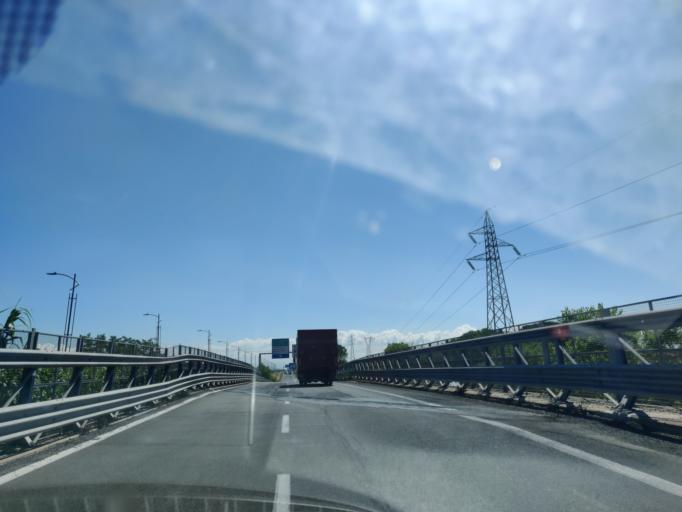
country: IT
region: Latium
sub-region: Citta metropolitana di Roma Capitale
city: Ponte Galeria-La Pisana
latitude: 41.8128
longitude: 12.3327
